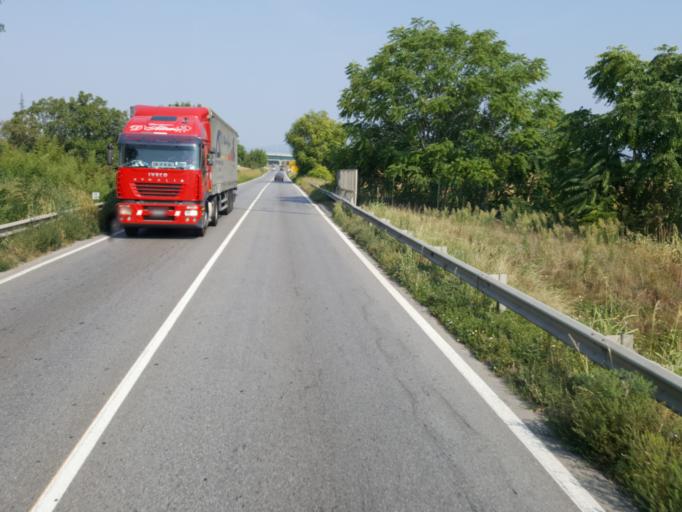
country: IT
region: Lombardy
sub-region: Provincia di Brescia
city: Travagliato
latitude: 45.5241
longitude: 10.0586
